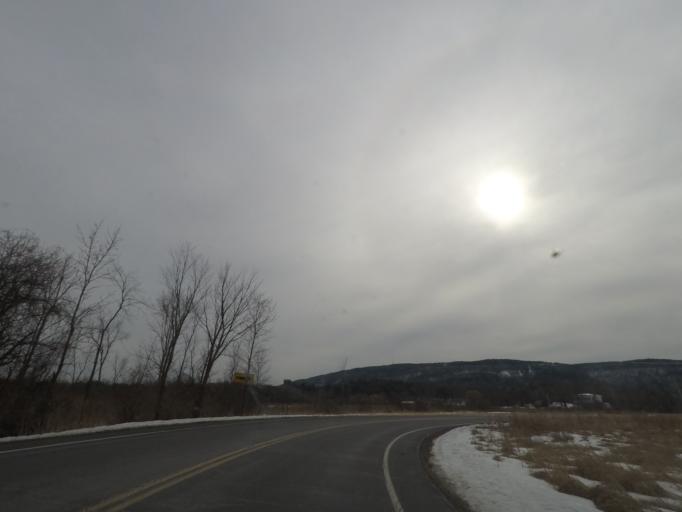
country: US
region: New York
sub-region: Albany County
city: Voorheesville
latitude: 42.6673
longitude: -73.9840
